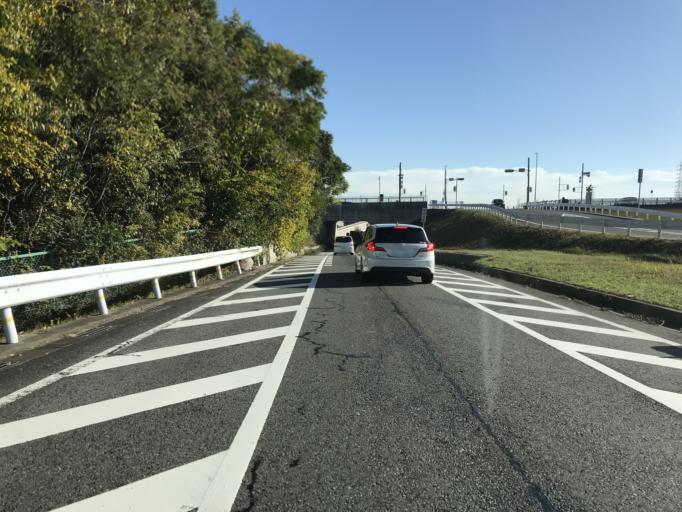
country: JP
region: Aichi
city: Kanie
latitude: 35.1482
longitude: 136.8307
